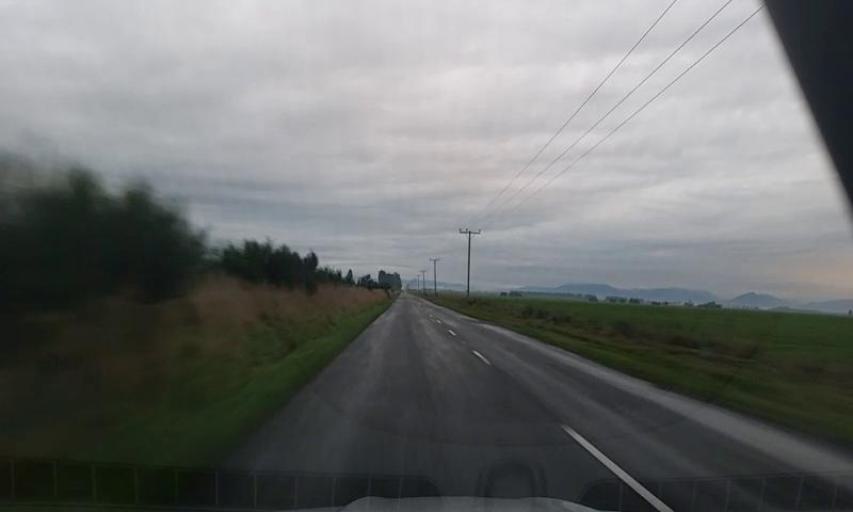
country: NZ
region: Canterbury
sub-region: Ashburton District
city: Rakaia
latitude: -43.7512
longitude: 171.8407
